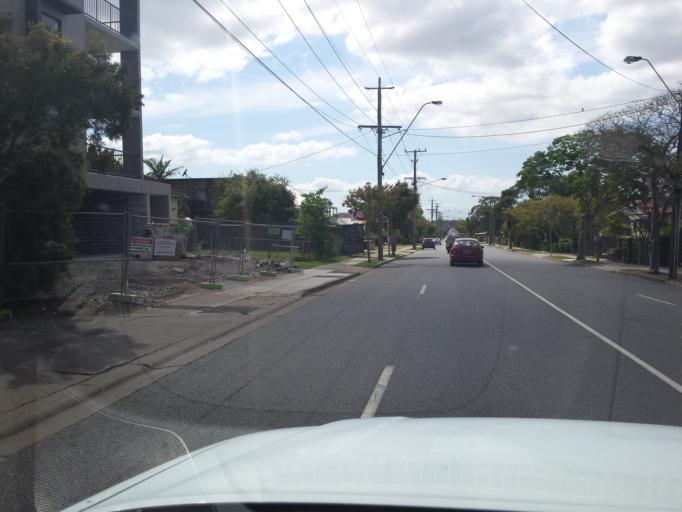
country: AU
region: Queensland
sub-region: Brisbane
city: Zillmere
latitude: -27.3595
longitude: 153.0387
